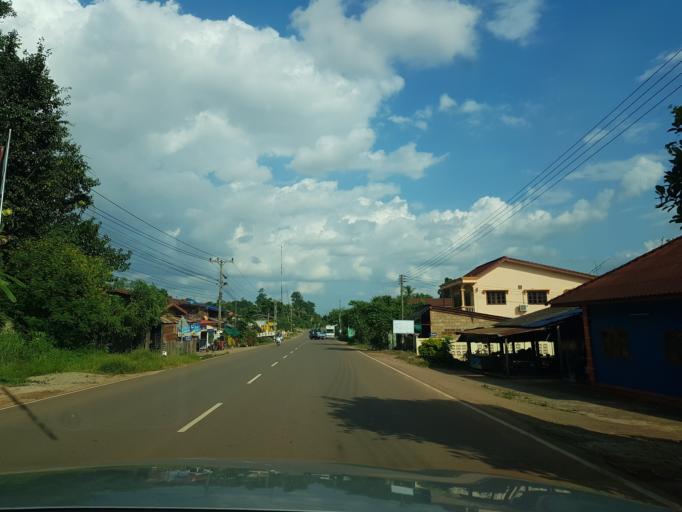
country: TH
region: Nong Khai
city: Si Chiang Mai
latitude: 17.9773
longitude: 102.4693
